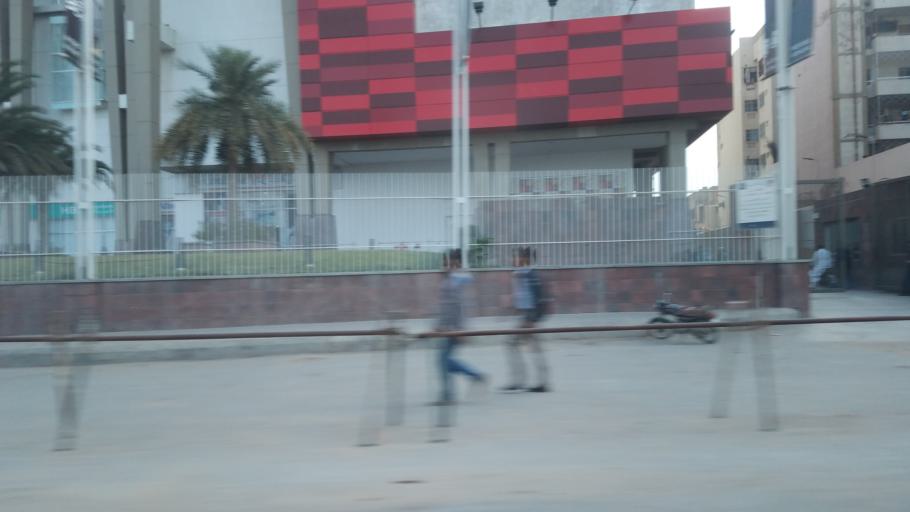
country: PK
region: Sindh
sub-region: Karachi District
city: Karachi
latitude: 24.9318
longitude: 67.0863
